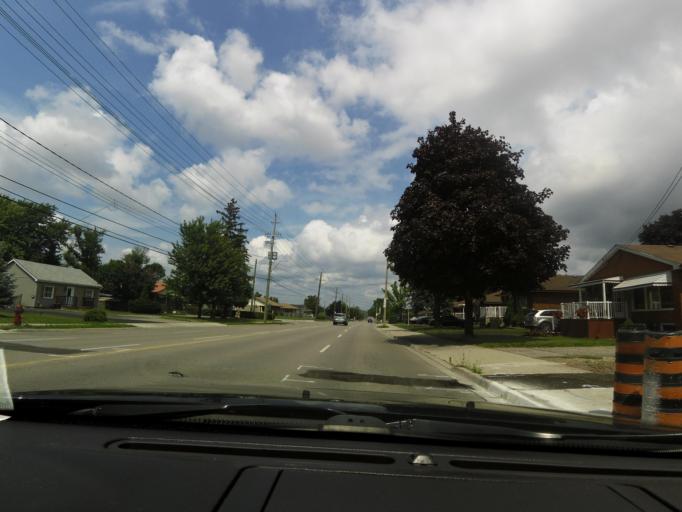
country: CA
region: Ontario
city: Hamilton
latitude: 43.2174
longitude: -79.8328
